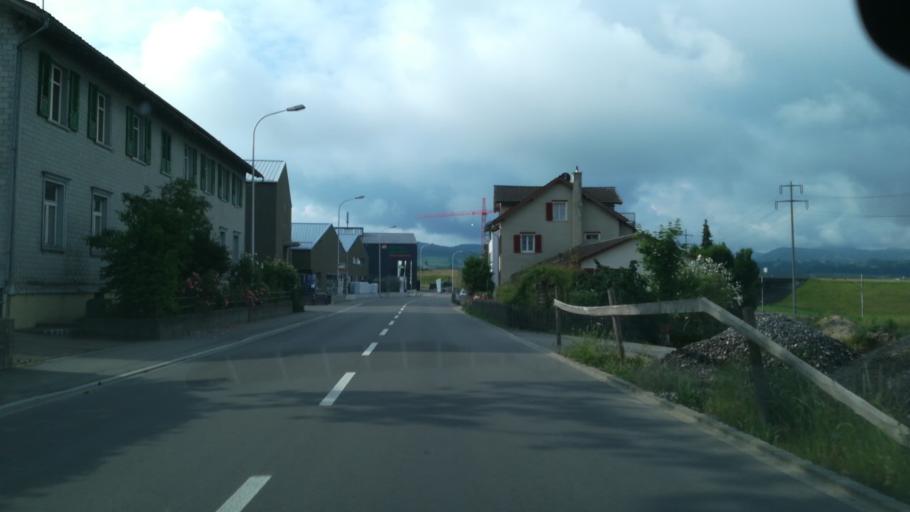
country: CH
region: Saint Gallen
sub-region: Wahlkreis St. Gallen
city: Gossau
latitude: 47.4275
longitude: 9.2412
